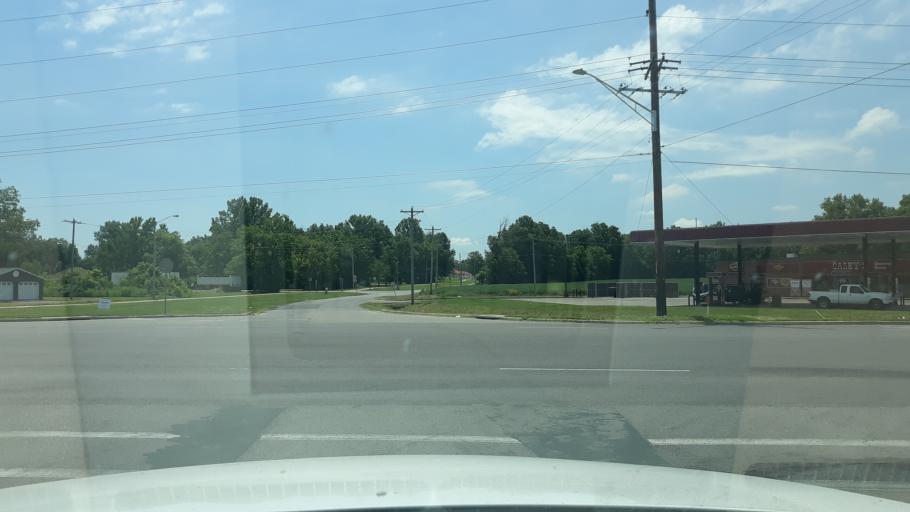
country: US
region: Illinois
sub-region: Saline County
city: Eldorado
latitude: 37.8090
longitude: -88.4346
